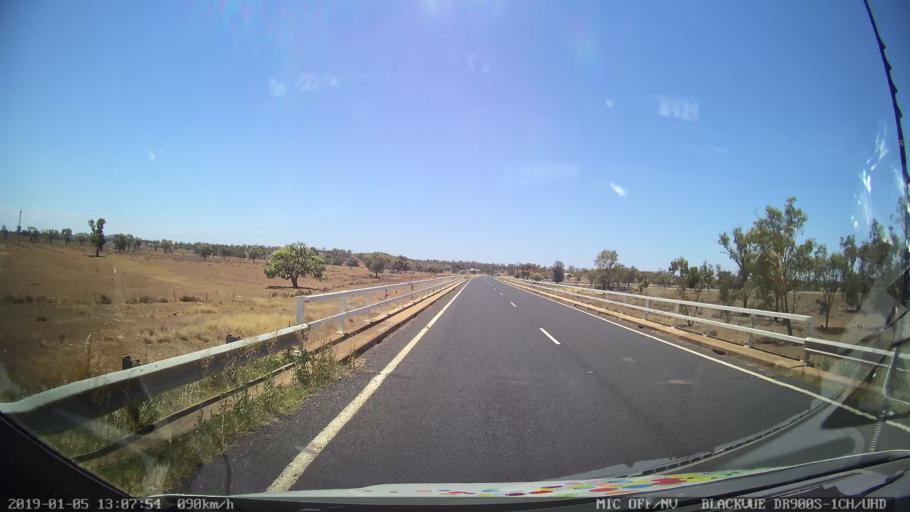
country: AU
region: New South Wales
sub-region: Gunnedah
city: Gunnedah
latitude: -31.0982
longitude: 149.8941
